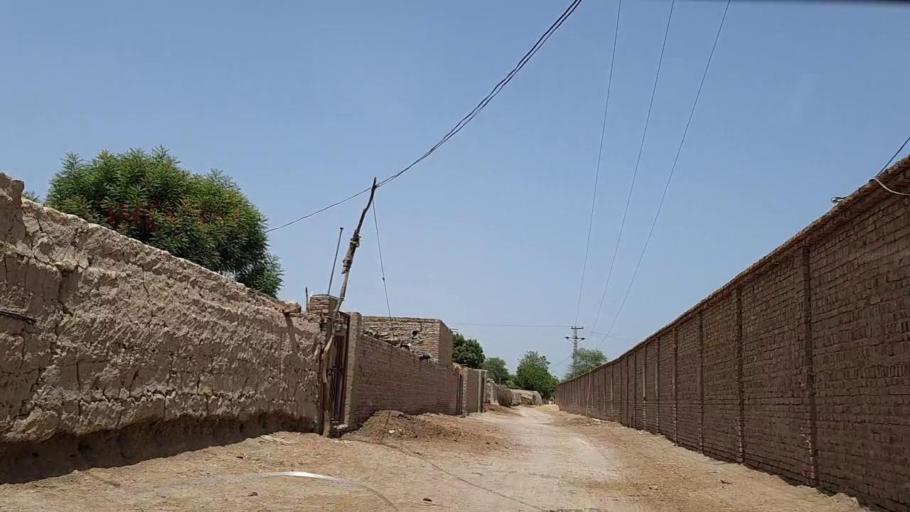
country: PK
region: Sindh
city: Tharu Shah
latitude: 26.9655
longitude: 68.0397
